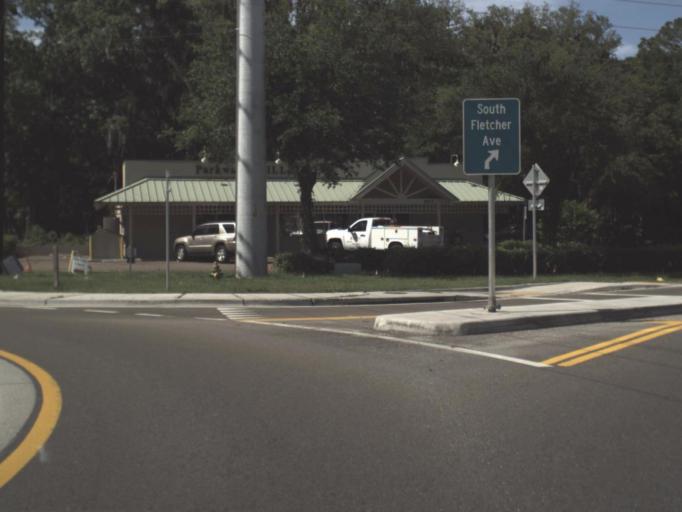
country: US
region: Florida
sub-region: Nassau County
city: Fernandina Beach
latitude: 30.5926
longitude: -81.4584
